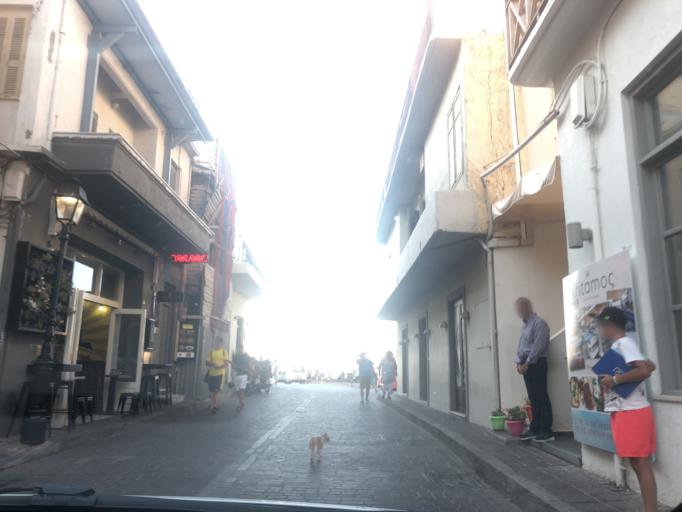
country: GR
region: Crete
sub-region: Nomos Rethymnis
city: Rethymno
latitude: 35.3705
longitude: 24.4759
